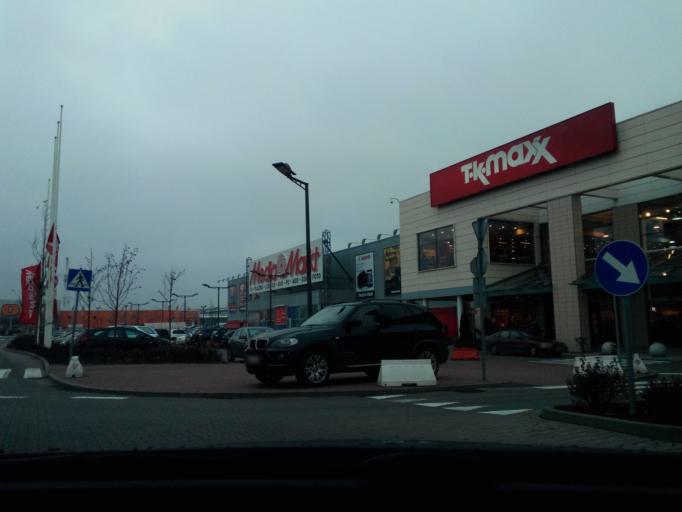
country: PL
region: Pomeranian Voivodeship
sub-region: Powiat gdanski
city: Kowale
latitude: 54.3733
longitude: 18.5195
